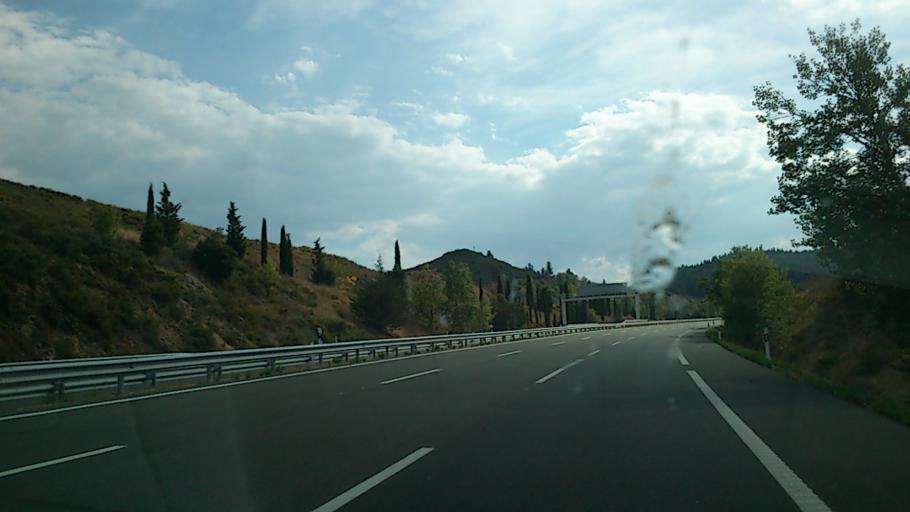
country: ES
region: La Rioja
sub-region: Provincia de La Rioja
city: Villalba de Rioja
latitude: 42.6306
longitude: -2.8569
